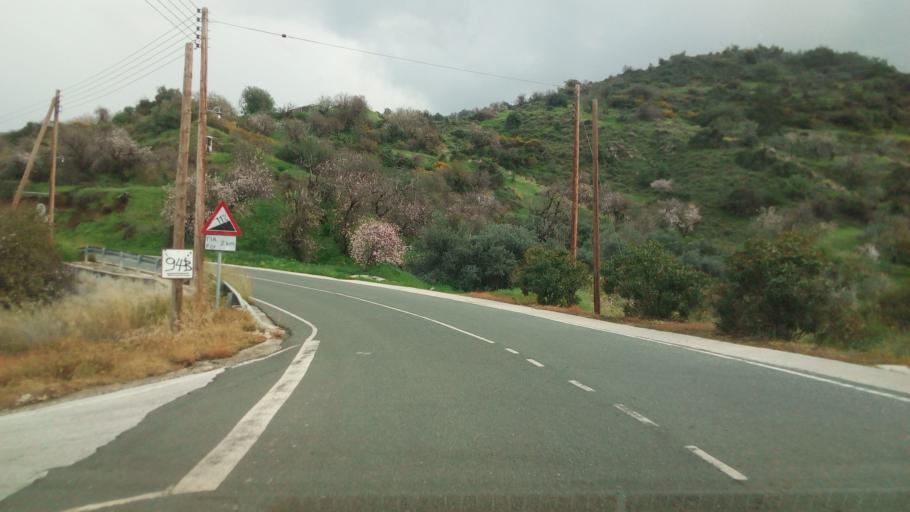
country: CY
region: Lefkosia
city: Kato Pyrgos
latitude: 35.1704
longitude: 32.5870
